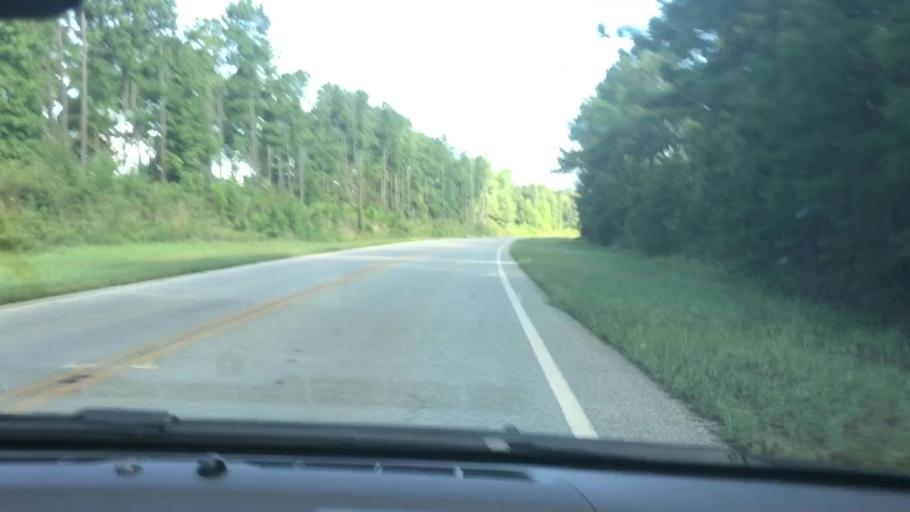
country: US
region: Georgia
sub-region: Clay County
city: Fort Gaines
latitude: 31.7422
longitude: -85.0528
